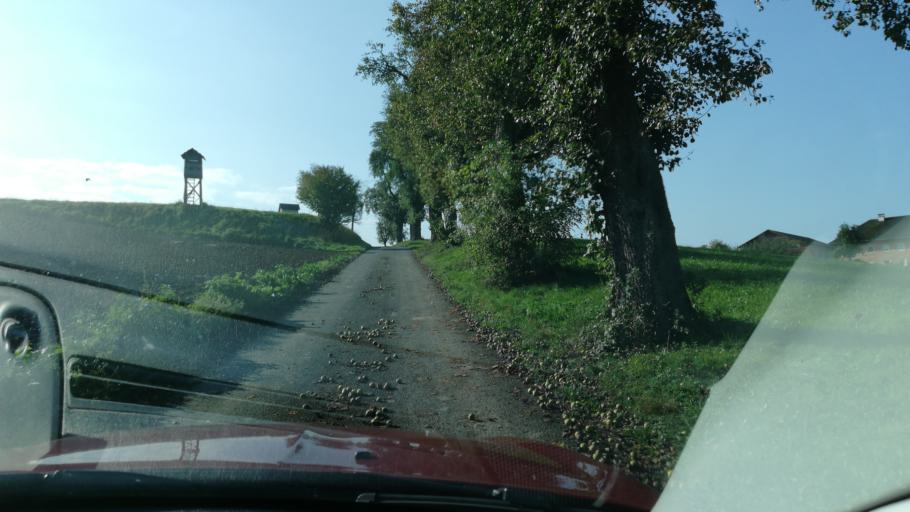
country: AT
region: Upper Austria
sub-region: Politischer Bezirk Kirchdorf an der Krems
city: Kremsmunster
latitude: 48.0966
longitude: 14.1672
